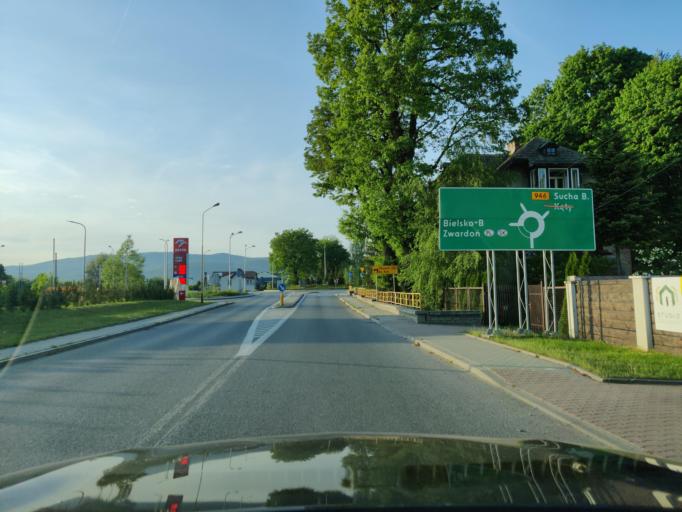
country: PL
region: Silesian Voivodeship
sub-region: Powiat zywiecki
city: Zywiec
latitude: 49.6994
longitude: 19.2019
